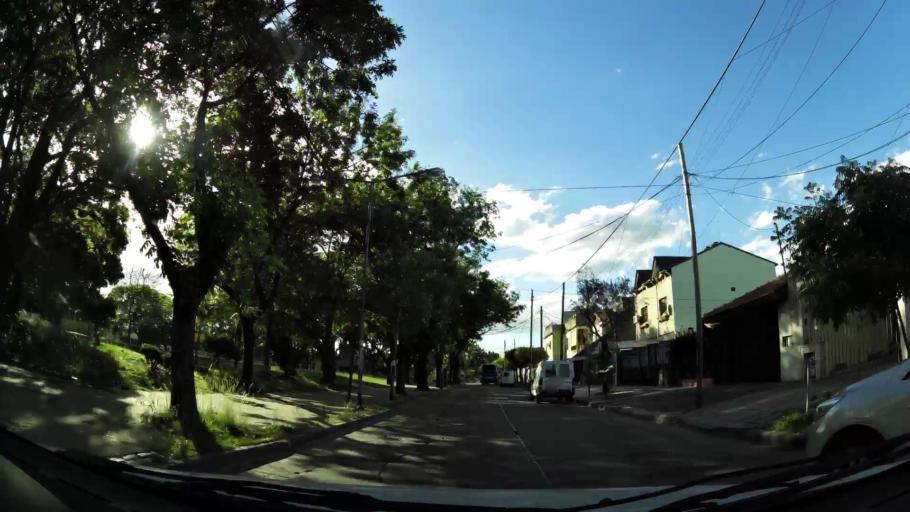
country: AR
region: Buenos Aires
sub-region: Partido de General San Martin
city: General San Martin
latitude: -34.5354
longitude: -58.5538
